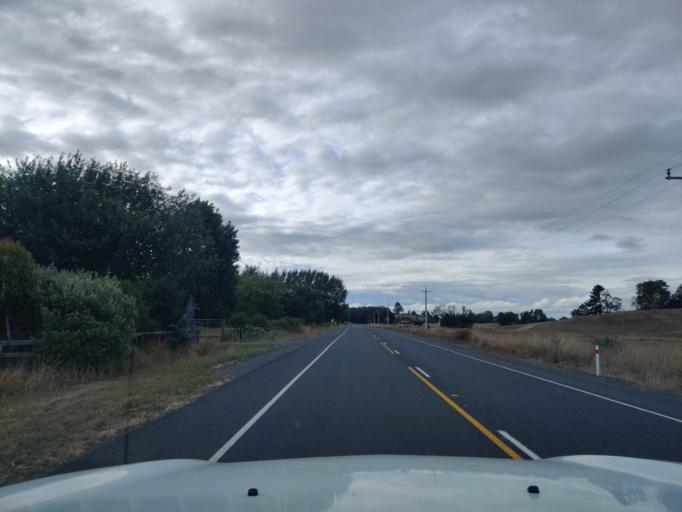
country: NZ
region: Waikato
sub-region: Waipa District
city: Cambridge
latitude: -37.8114
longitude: 175.4528
